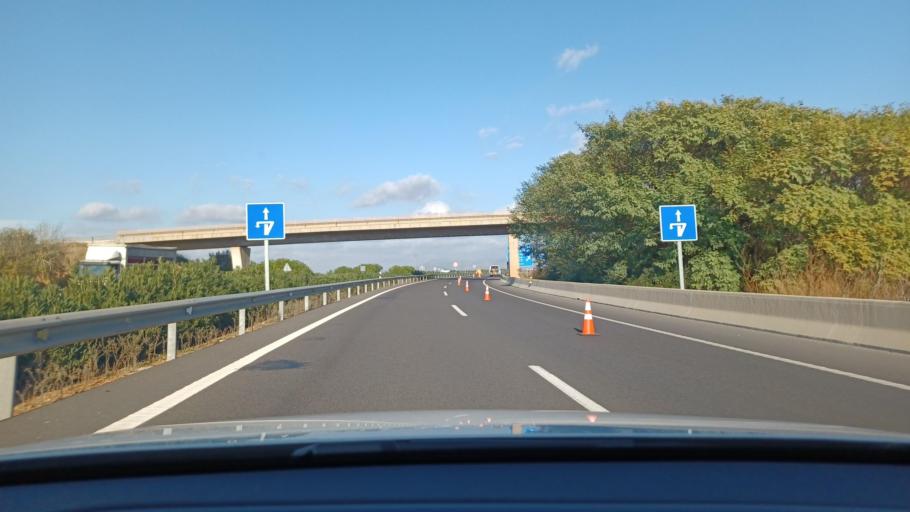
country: ES
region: Valencia
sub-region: Provincia de Castello
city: Betxi
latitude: 39.9208
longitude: -0.1953
